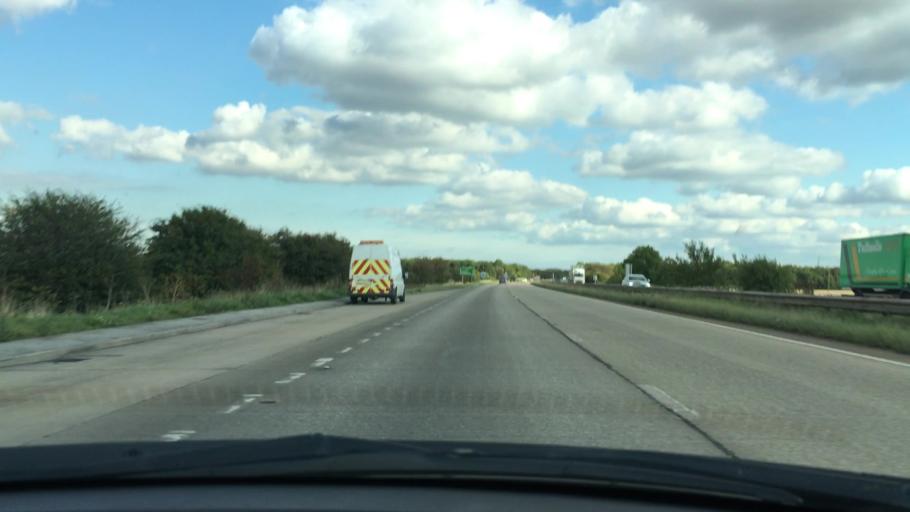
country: GB
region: England
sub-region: North East Lincolnshire
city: Healing
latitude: 53.5957
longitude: -0.1820
